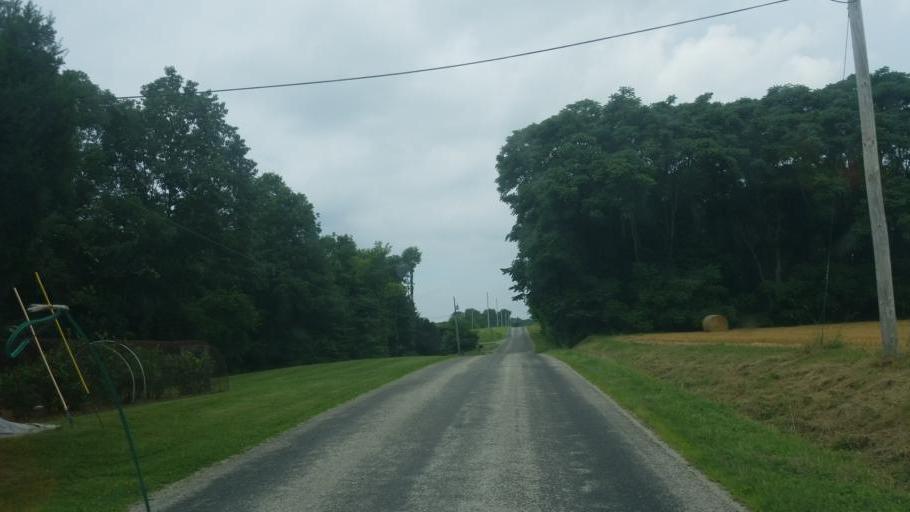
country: US
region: Ohio
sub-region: Wayne County
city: Wooster
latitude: 40.8794
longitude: -81.9933
